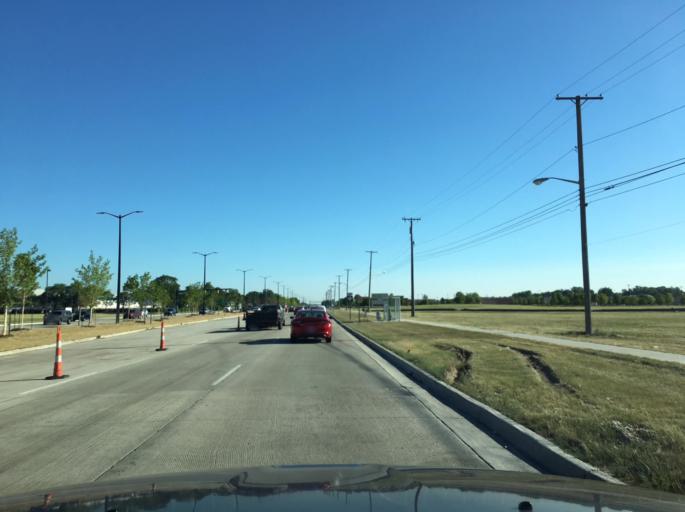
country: US
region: Michigan
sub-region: Macomb County
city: Sterling Heights
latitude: 42.5514
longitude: -83.0288
